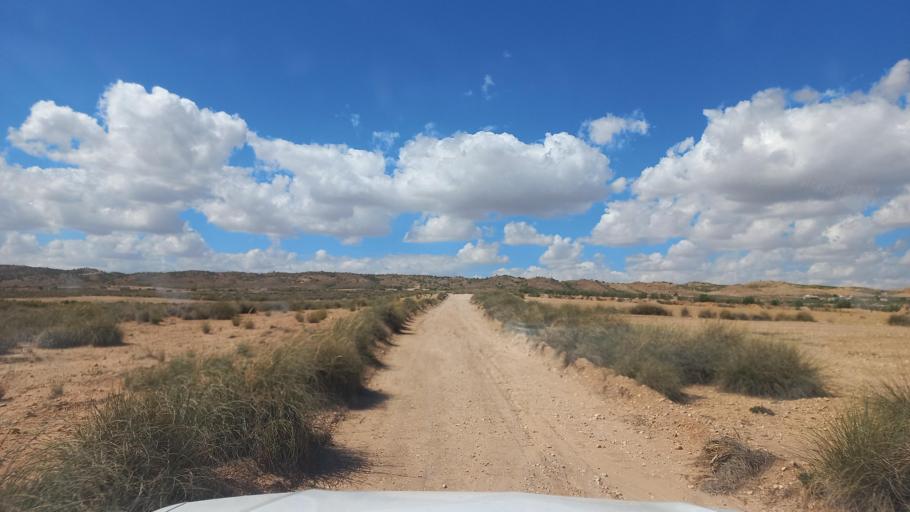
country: TN
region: Al Qasrayn
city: Sbiba
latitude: 35.3588
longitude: 9.0072
